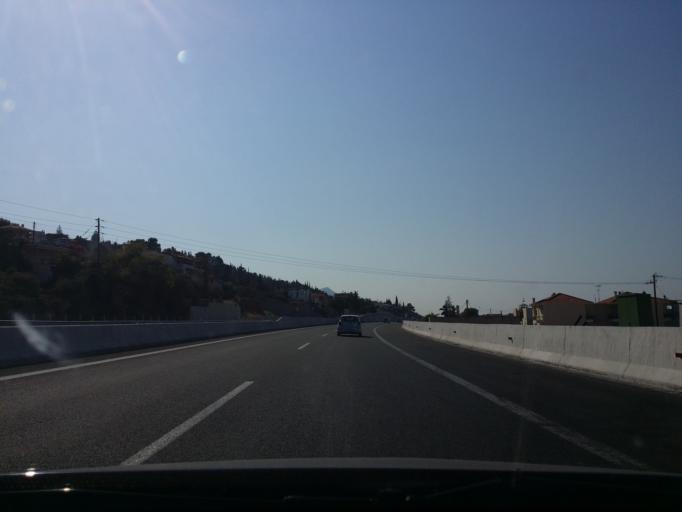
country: GR
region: Peloponnese
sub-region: Nomos Korinthias
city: Kato Dhiminio
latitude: 38.0446
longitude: 22.6963
